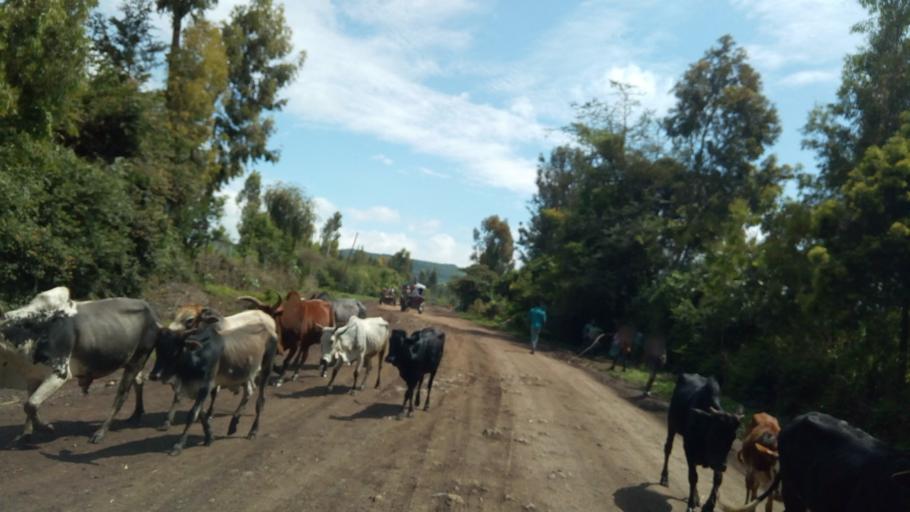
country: ET
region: Oromiya
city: Bishoftu
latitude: 8.8462
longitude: 39.0174
